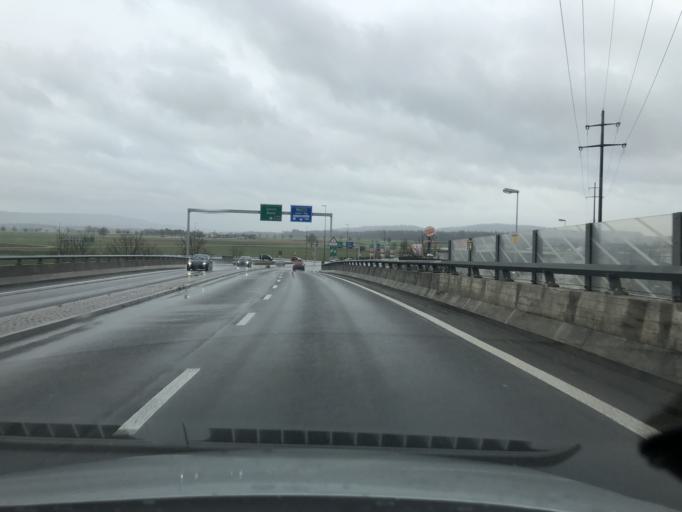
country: CH
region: Aargau
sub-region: Bezirk Brugg
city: Hausen
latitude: 47.4519
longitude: 8.2136
